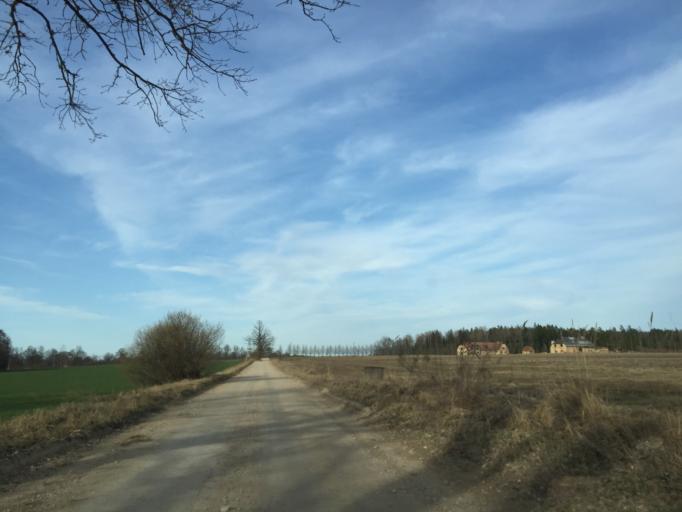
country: LV
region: Kegums
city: Kegums
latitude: 56.7968
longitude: 24.7633
